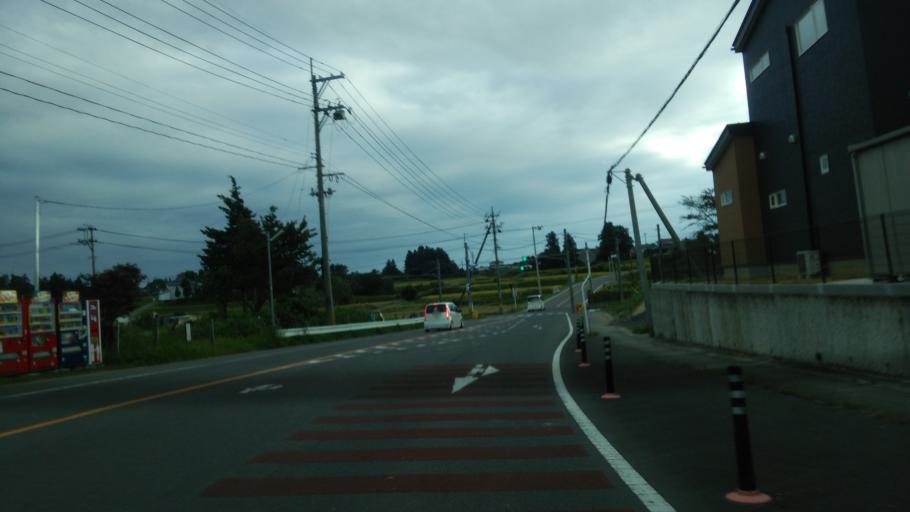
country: JP
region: Fukushima
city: Koriyama
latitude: 37.3509
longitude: 140.3399
